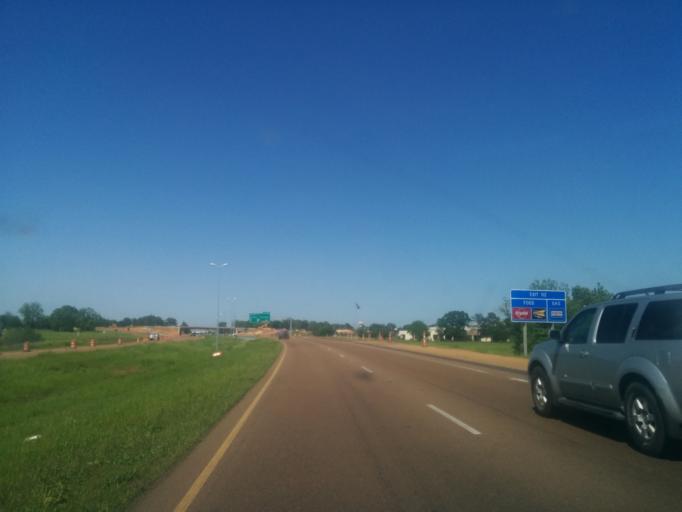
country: US
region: Mississippi
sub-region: Madison County
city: Madison
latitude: 32.5122
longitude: -90.1050
